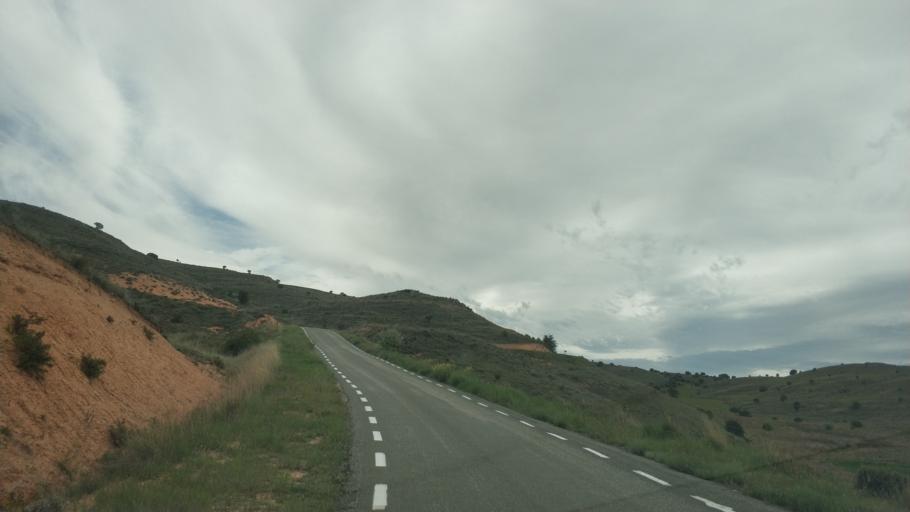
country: ES
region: Castille and Leon
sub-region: Provincia de Soria
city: Caltojar
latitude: 41.4207
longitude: -2.7872
